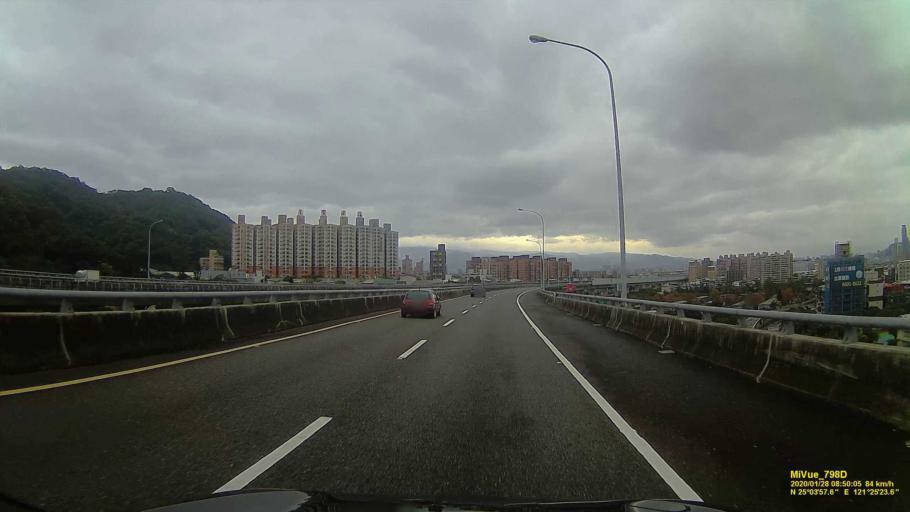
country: TW
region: Taipei
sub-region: Taipei
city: Banqiao
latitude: 25.0660
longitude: 121.4237
